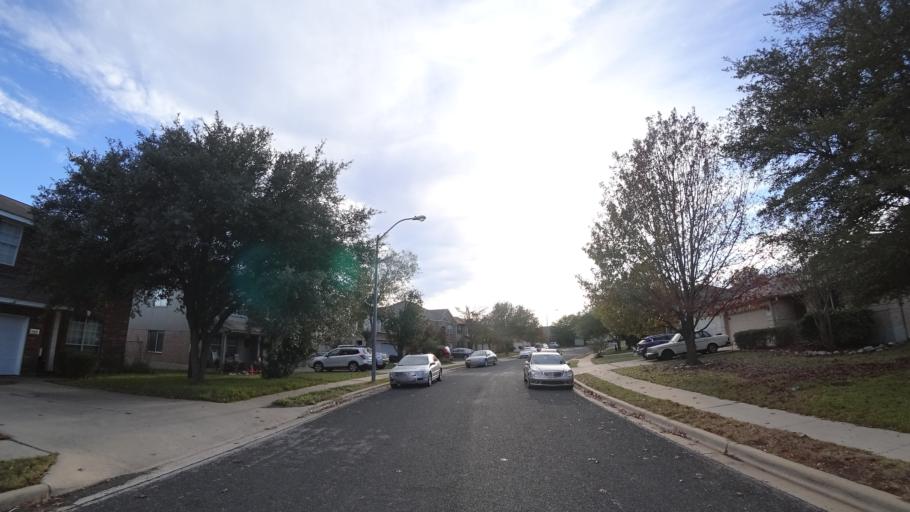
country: US
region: Texas
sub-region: Williamson County
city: Brushy Creek
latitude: 30.5001
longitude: -97.7297
